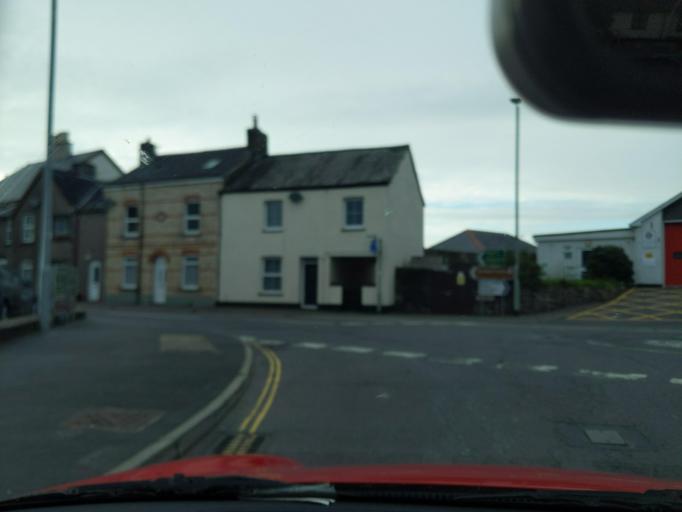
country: GB
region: England
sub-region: Devon
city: Great Torrington
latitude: 50.9535
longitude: -4.1409
